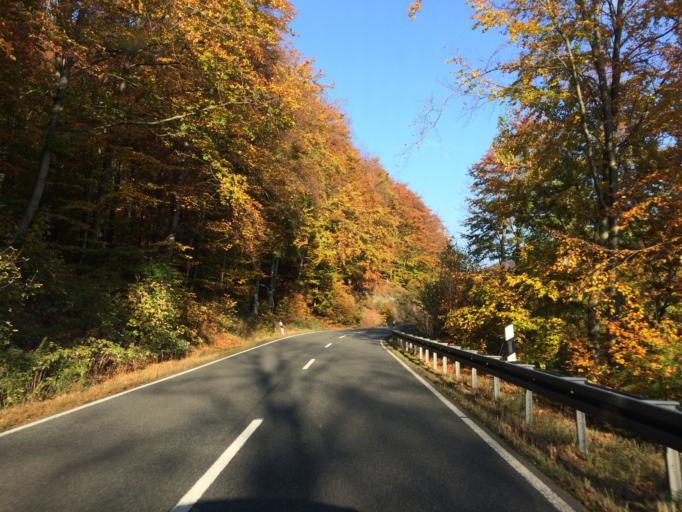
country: DE
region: Lower Saxony
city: Sankt Andreasberg
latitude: 51.6624
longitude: 10.5261
